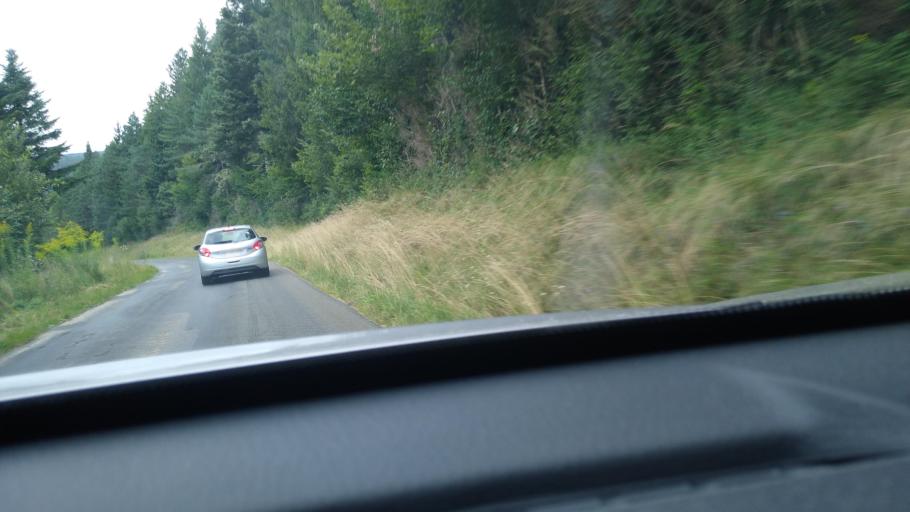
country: FR
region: Rhone-Alpes
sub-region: Departement de l'Ain
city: Saint-Martin-du-Frene
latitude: 46.1315
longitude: 5.5600
